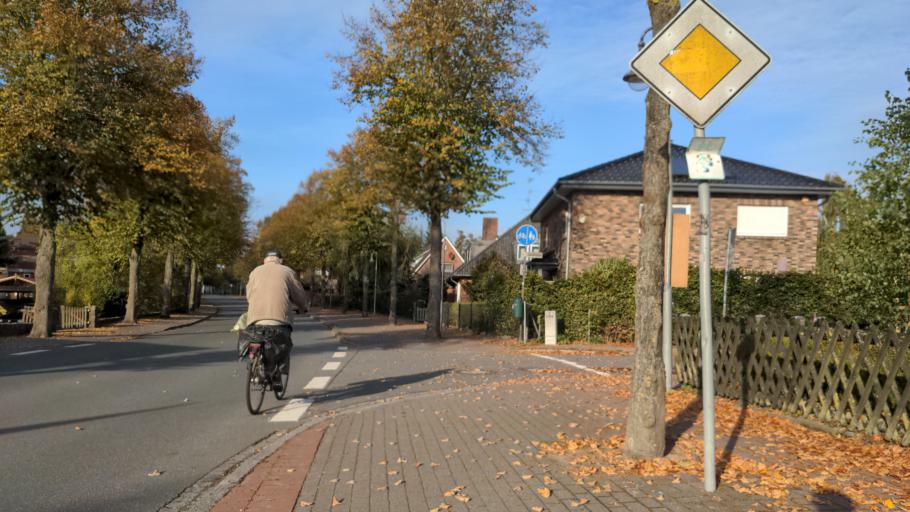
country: DE
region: Schleswig-Holstein
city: Lensahn
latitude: 54.2159
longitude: 10.8834
